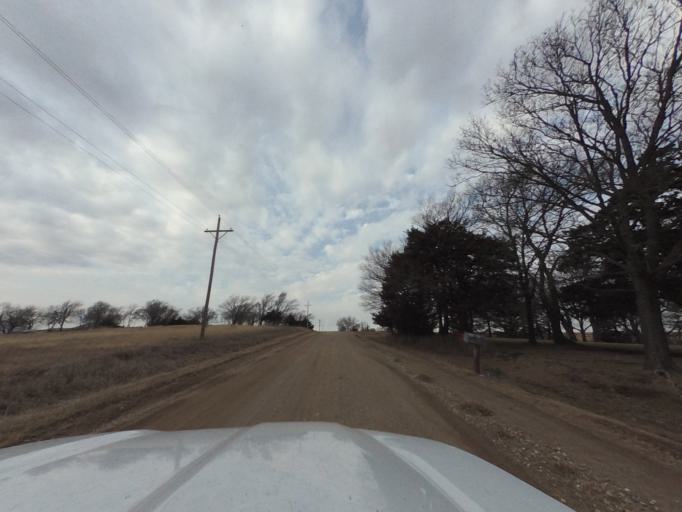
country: US
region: Kansas
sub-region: Chase County
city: Cottonwood Falls
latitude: 38.4492
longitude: -96.3708
